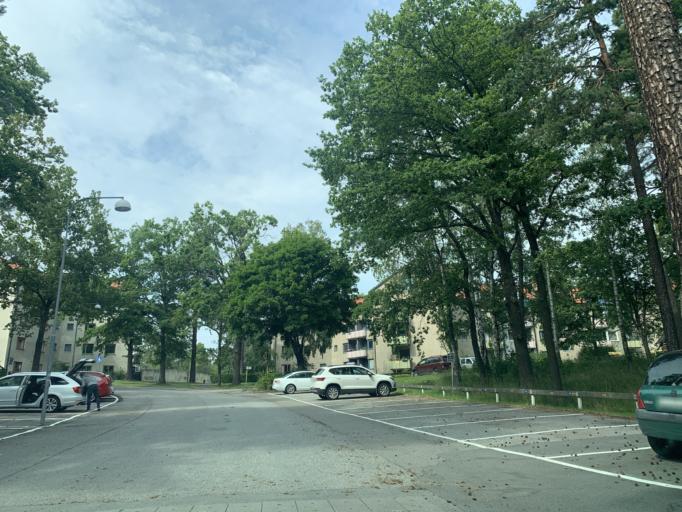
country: SE
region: Stockholm
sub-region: Norrtalje Kommun
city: Bergshamra
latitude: 59.3807
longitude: 18.0309
